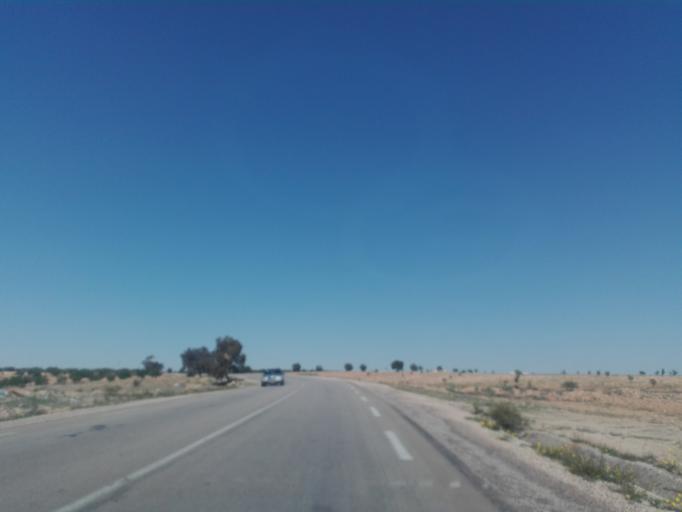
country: TN
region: Safaqis
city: Bi'r `Ali Bin Khalifah
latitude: 34.7458
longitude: 10.3613
